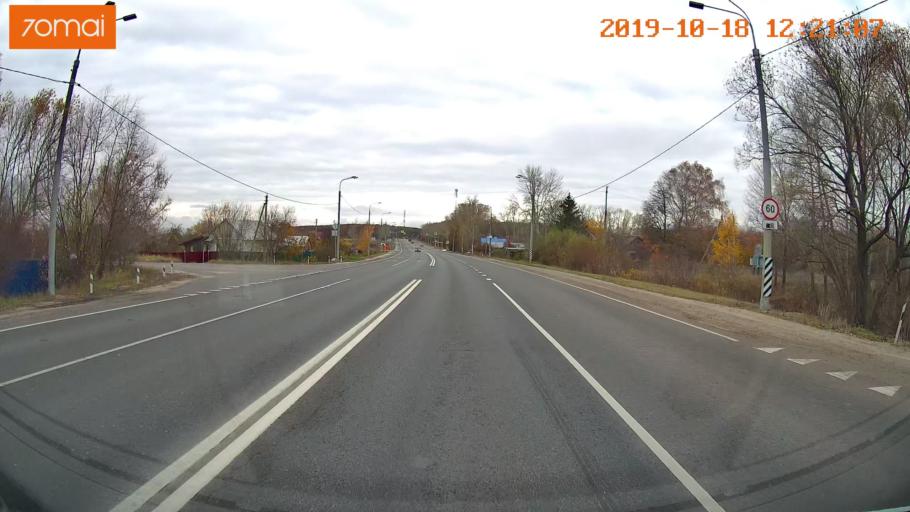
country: RU
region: Rjazan
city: Bagramovo
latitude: 54.5068
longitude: 39.4870
